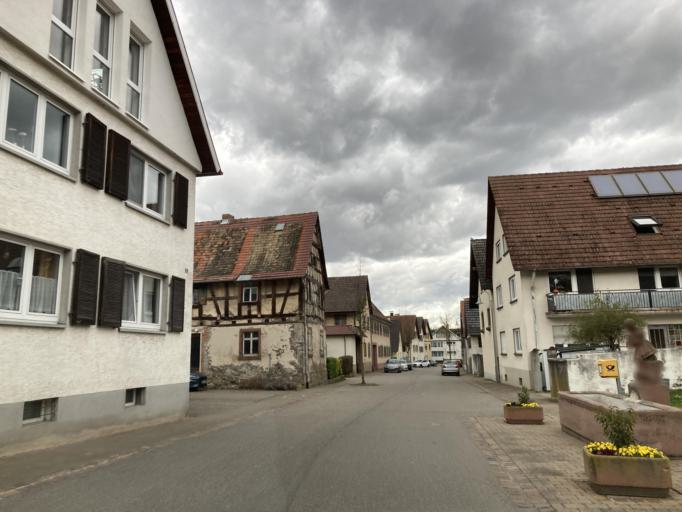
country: DE
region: Baden-Wuerttemberg
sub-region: Freiburg Region
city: Vogtsburg
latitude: 48.1250
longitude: 7.6552
